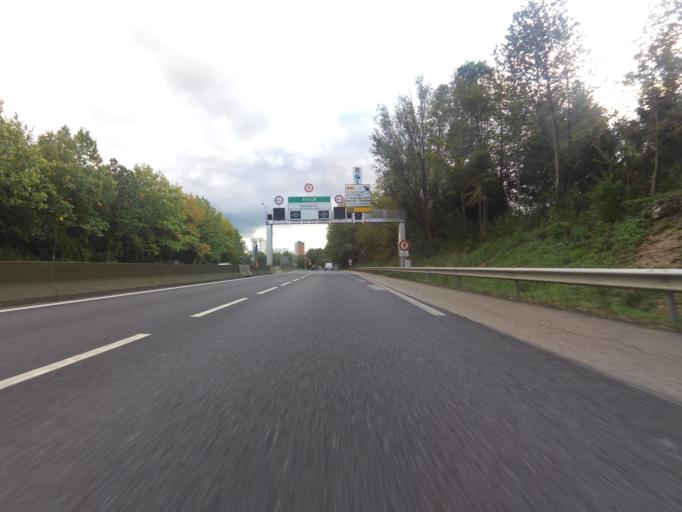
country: FR
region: Haute-Normandie
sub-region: Departement de la Seine-Maritime
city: Bois-Guillaume
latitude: 49.4702
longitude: 1.1335
